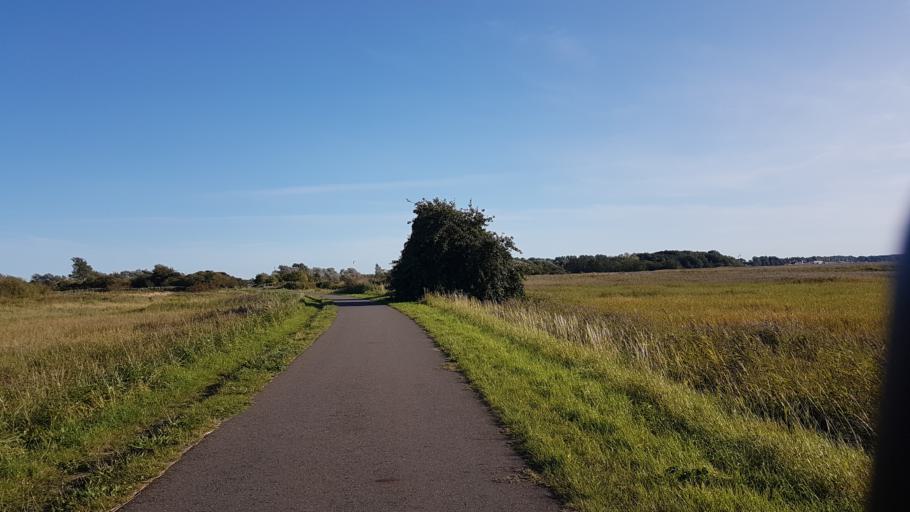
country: DE
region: Mecklenburg-Vorpommern
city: Wiek
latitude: 54.6413
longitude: 13.2883
